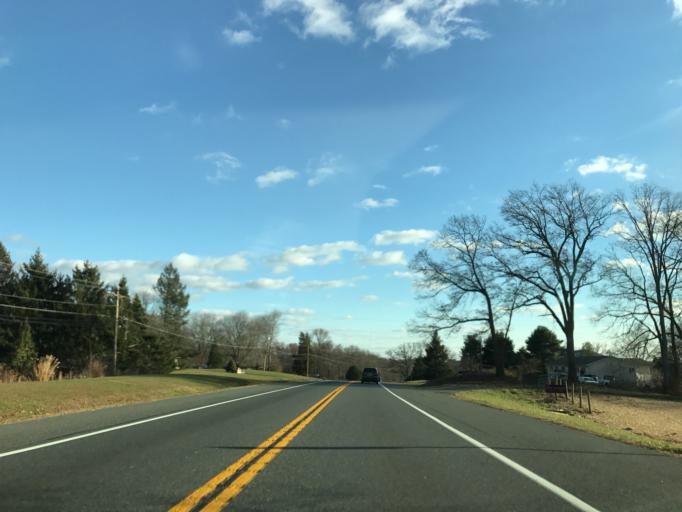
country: US
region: Maryland
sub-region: Harford County
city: Joppatowne
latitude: 39.4557
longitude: -76.3583
